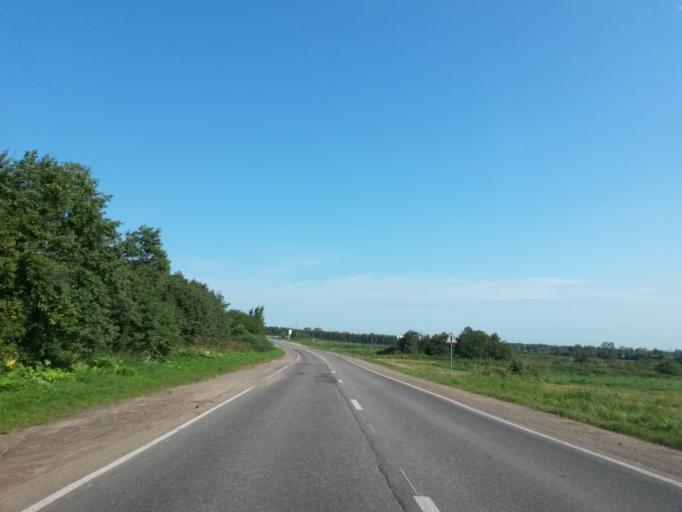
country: RU
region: Jaroslavl
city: Yaroslavl
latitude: 57.5479
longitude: 39.8619
